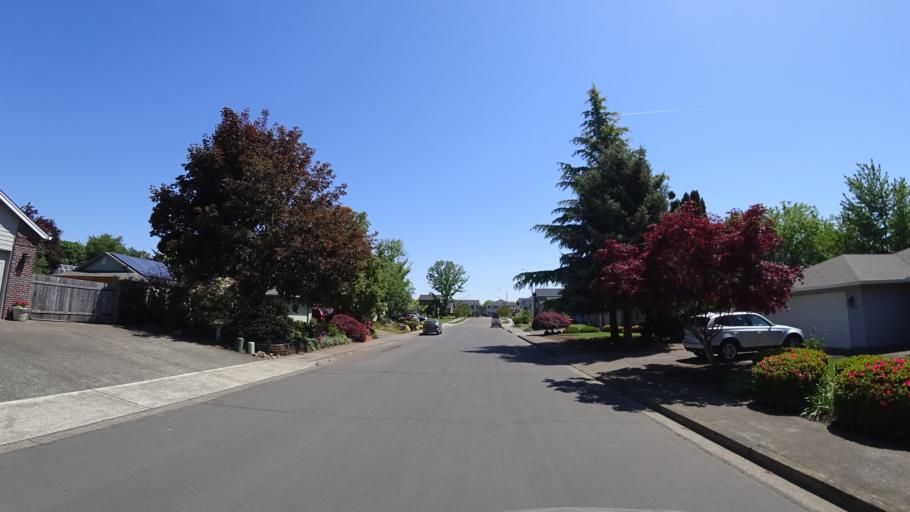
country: US
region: Oregon
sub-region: Washington County
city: Rockcreek
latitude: 45.5357
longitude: -122.9210
